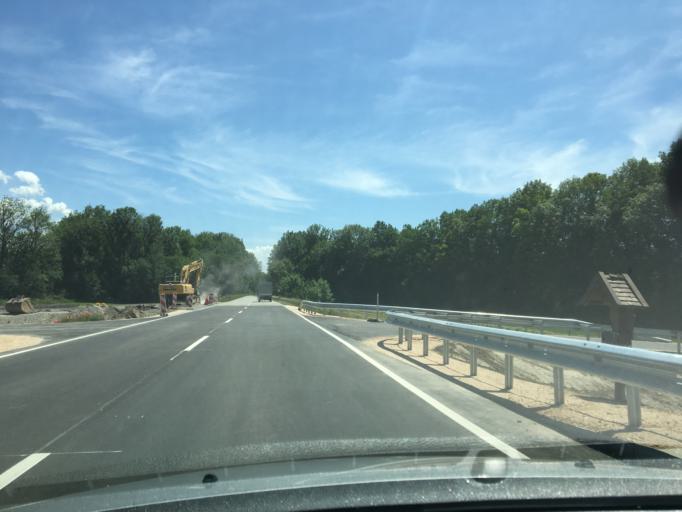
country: DE
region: Bavaria
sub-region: Upper Bavaria
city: Freilassing
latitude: 47.8735
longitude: 12.9731
